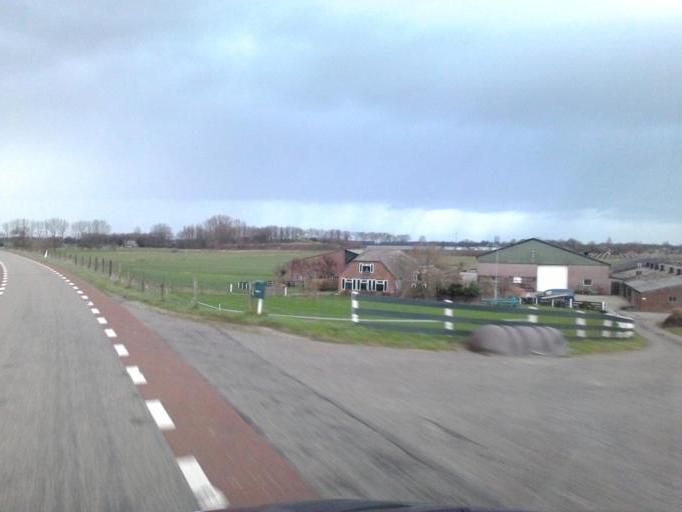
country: NL
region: Utrecht
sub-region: Gemeente Houten
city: Houten
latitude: 51.9726
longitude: 5.1654
